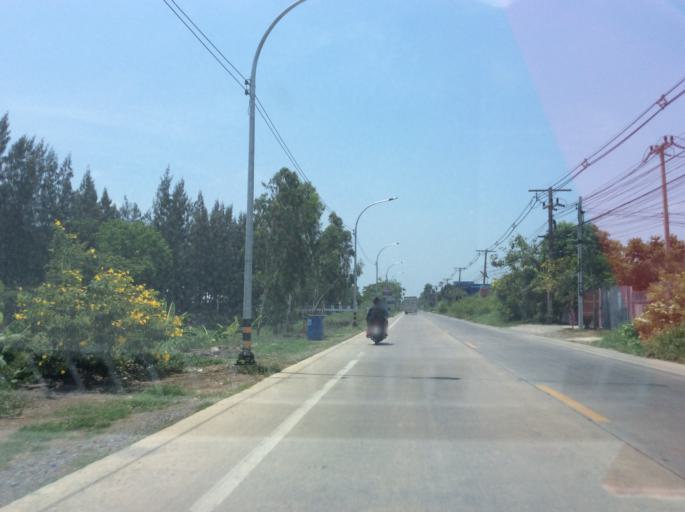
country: TH
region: Pathum Thani
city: Ban Rangsit
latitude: 14.0258
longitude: 100.7786
